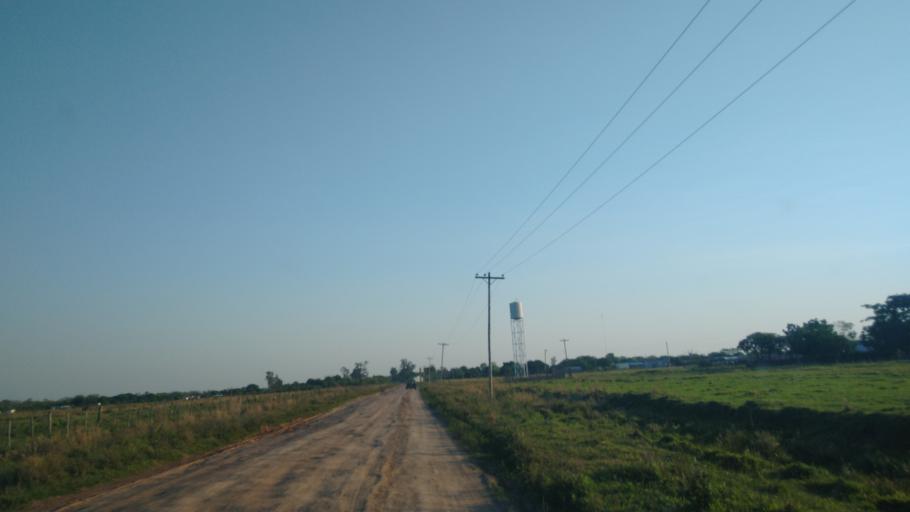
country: PY
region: Neembucu
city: Cerrito
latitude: -27.3800
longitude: -57.6560
